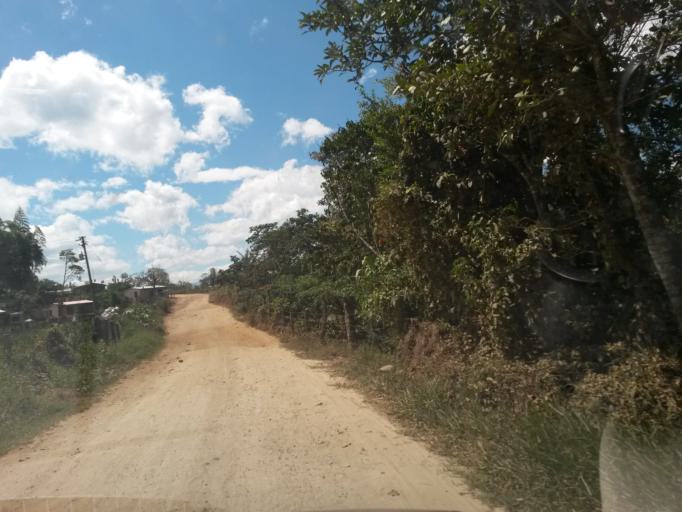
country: CO
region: Cauca
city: Morales
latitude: 2.7463
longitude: -76.6290
